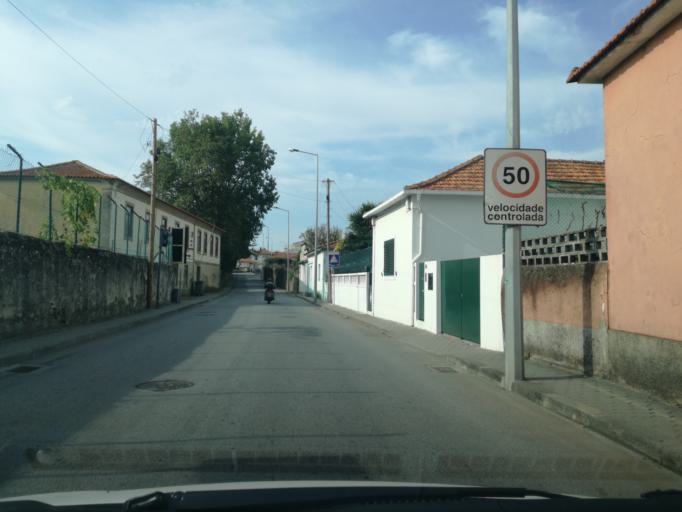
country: PT
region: Porto
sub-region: Vila Nova de Gaia
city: Sao Felix da Marinha
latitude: 41.0436
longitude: -8.6282
